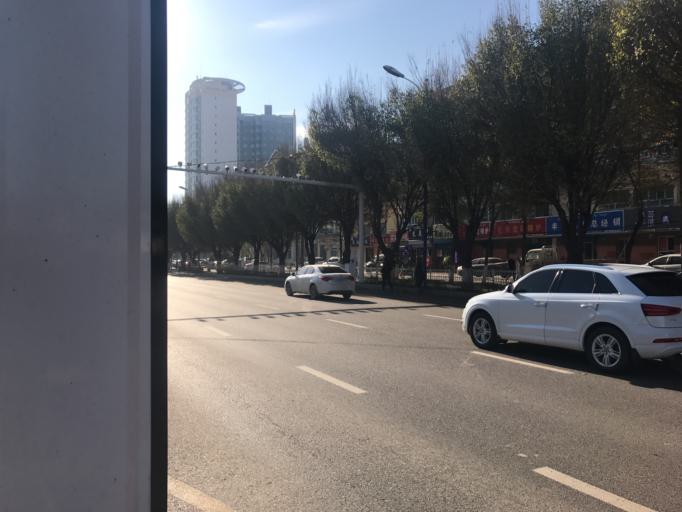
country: CN
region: Xinjiang Uygur Zizhiqu
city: Taxkowruek
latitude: 43.9329
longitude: 81.2992
